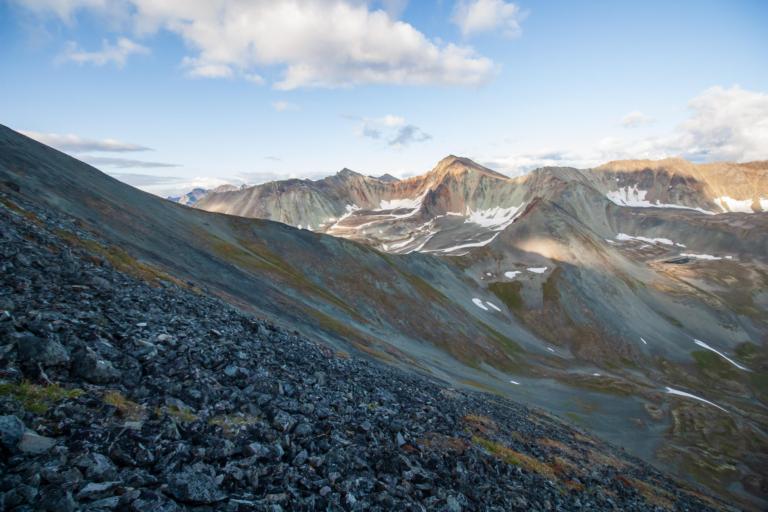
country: RU
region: Kamtsjatka
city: Yelizovo
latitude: 53.8572
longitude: 158.1928
